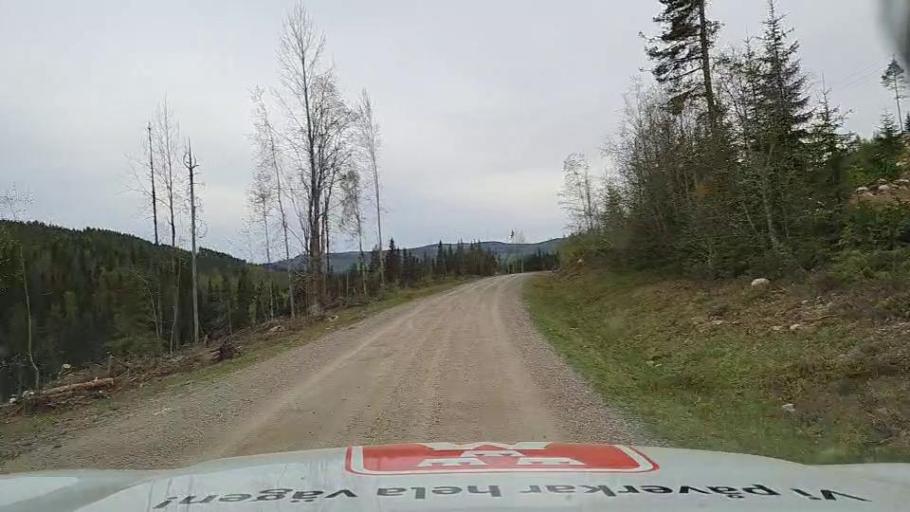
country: SE
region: Jaemtland
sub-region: Bergs Kommun
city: Hoverberg
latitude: 62.5274
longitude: 14.7115
